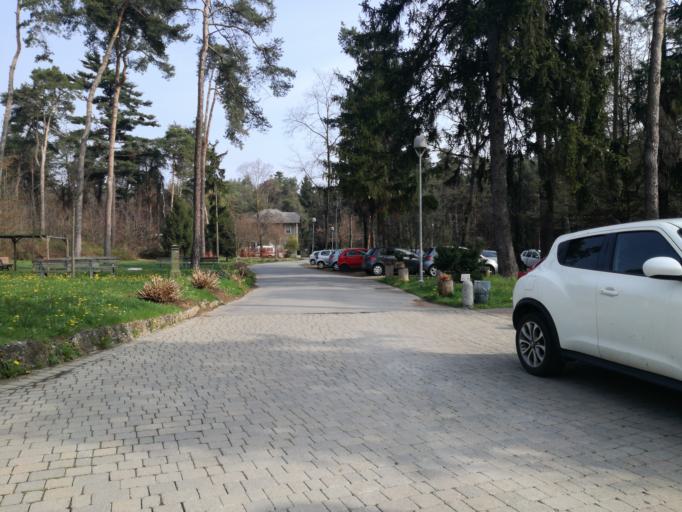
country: IT
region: Lombardy
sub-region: Citta metropolitana di Milano
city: Cambiago
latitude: 45.5923
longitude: 9.4317
